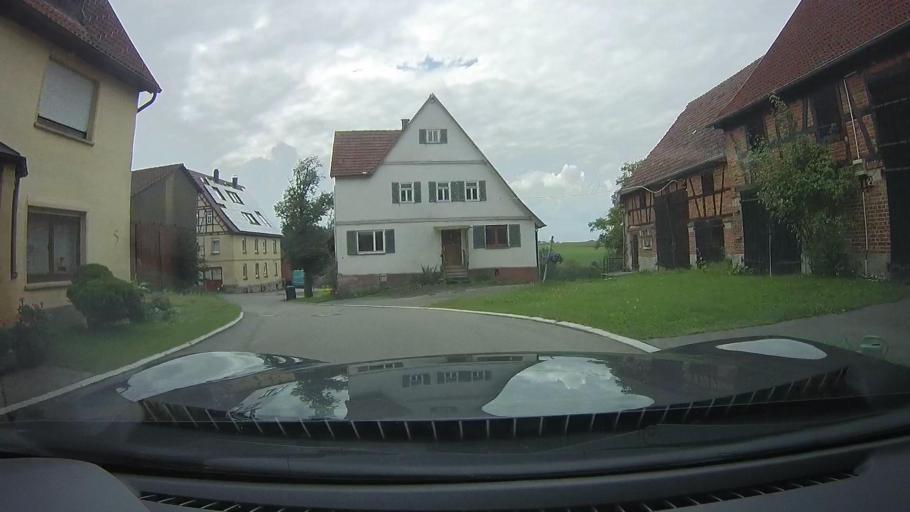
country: DE
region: Baden-Wuerttemberg
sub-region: Regierungsbezirk Stuttgart
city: Murrhardt
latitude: 48.9536
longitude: 9.5527
